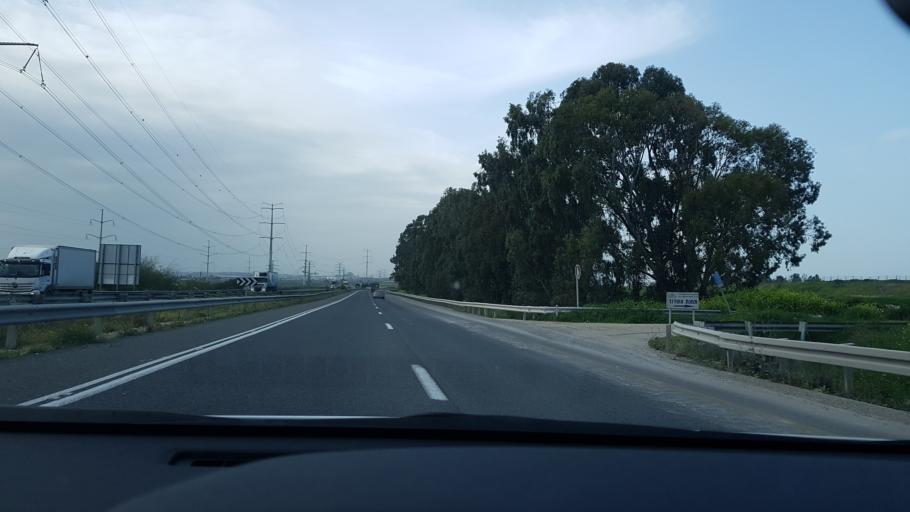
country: IL
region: Central District
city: Gan Yavne
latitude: 31.7985
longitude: 34.6880
